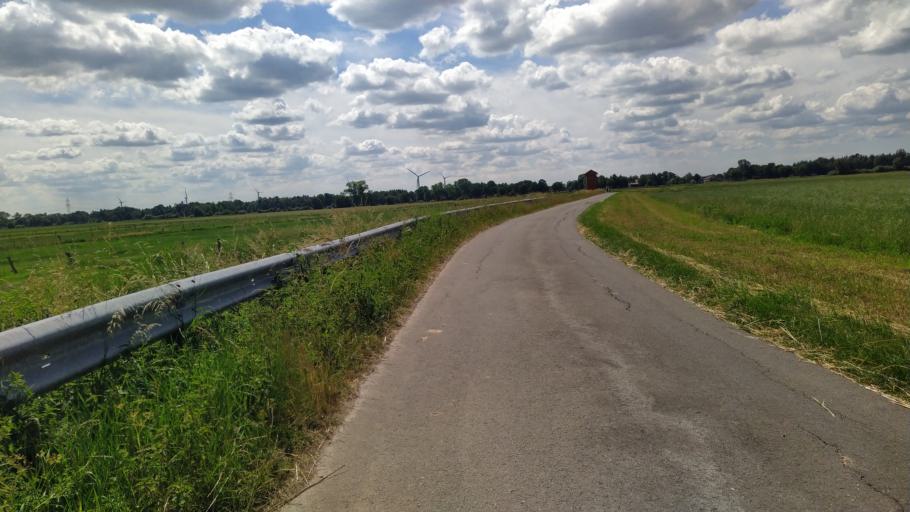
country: DE
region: Lower Saxony
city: Estorf
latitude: 53.5748
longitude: 9.1628
